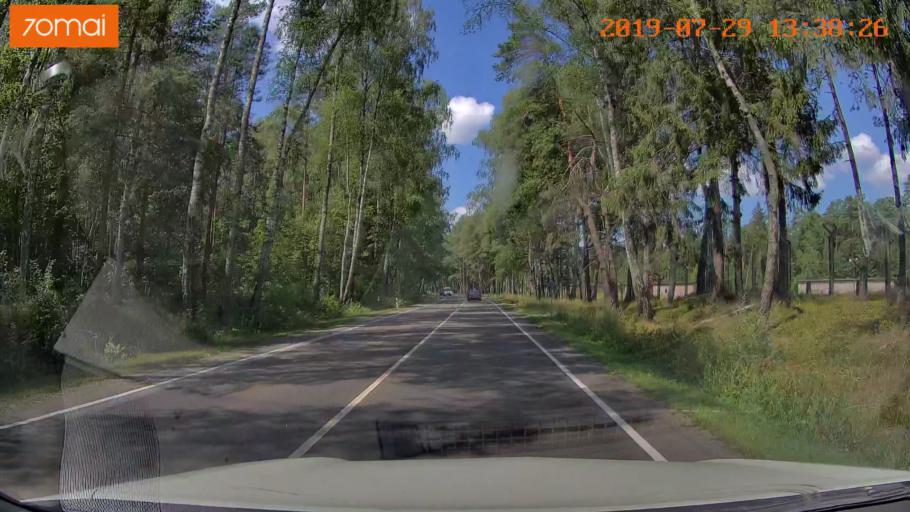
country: RU
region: Kaliningrad
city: Volochayevskoye
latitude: 54.7211
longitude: 20.1710
